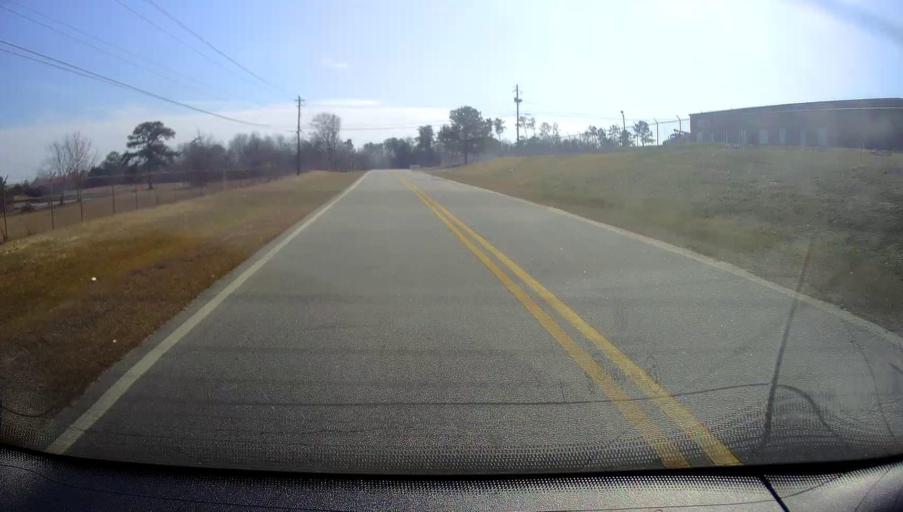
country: US
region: Georgia
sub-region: Bibb County
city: West Point
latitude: 32.8175
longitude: -83.7263
